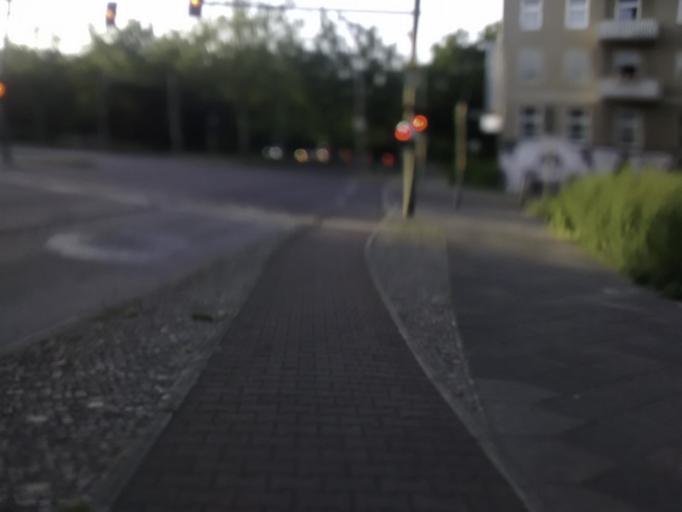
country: DE
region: Berlin
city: Reinickendorf
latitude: 52.5755
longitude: 13.3481
